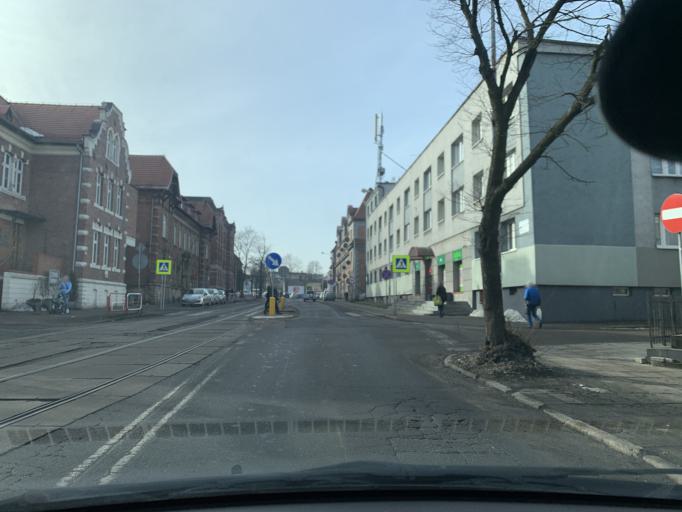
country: PL
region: Silesian Voivodeship
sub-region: Ruda Slaska
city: Ruda Slaska
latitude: 50.3144
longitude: 18.8523
